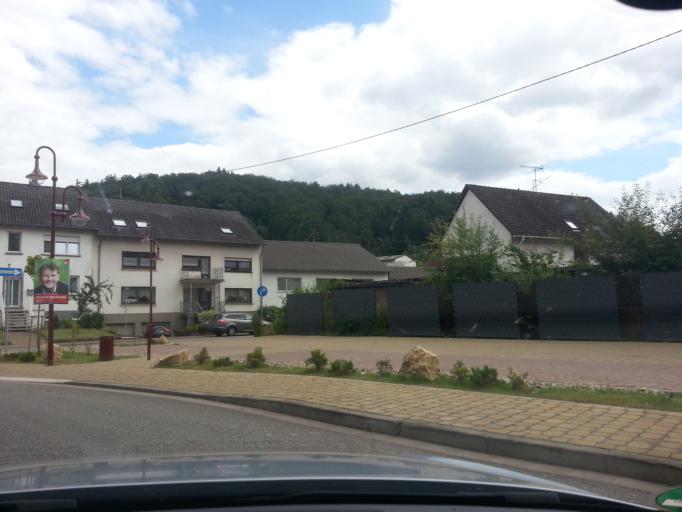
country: DE
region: Saarland
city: Beckingen
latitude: 49.4287
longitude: 6.7310
